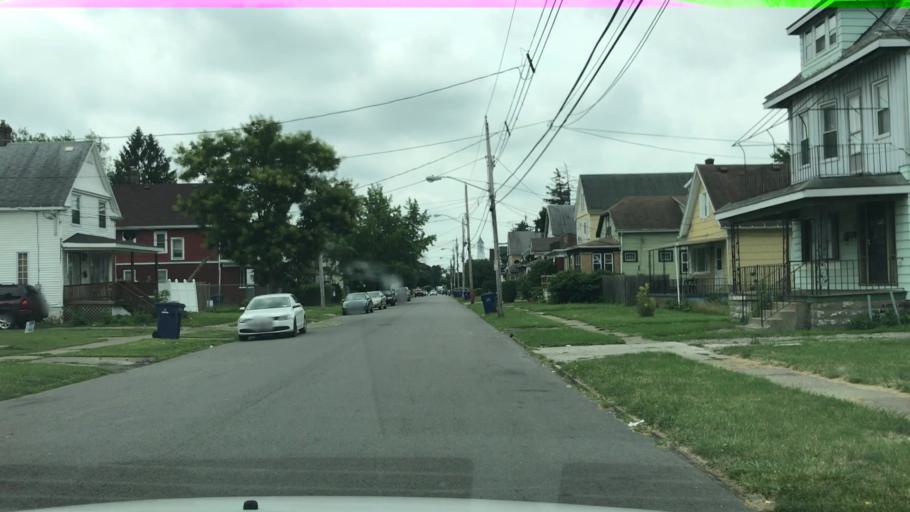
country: US
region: New York
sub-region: Erie County
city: Sloan
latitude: 42.9258
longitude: -78.8022
